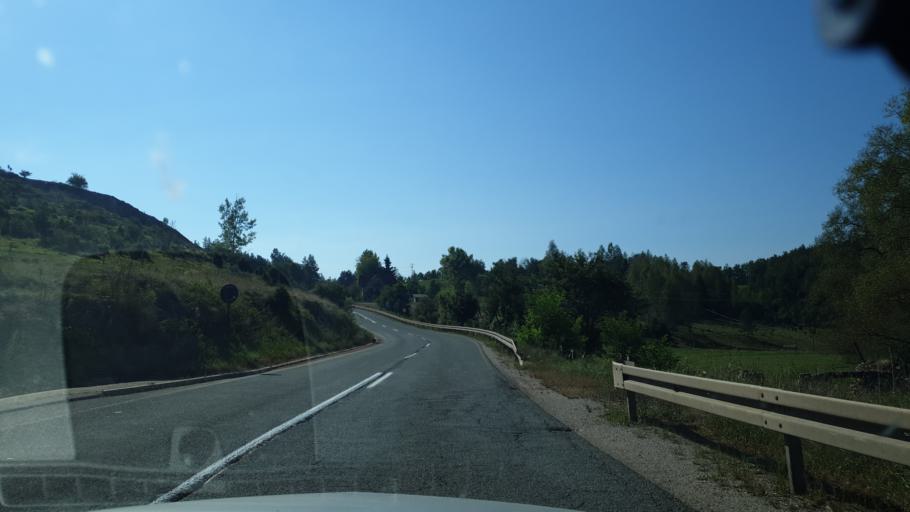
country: RS
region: Central Serbia
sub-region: Zlatiborski Okrug
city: Nova Varos
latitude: 43.5437
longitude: 19.7872
